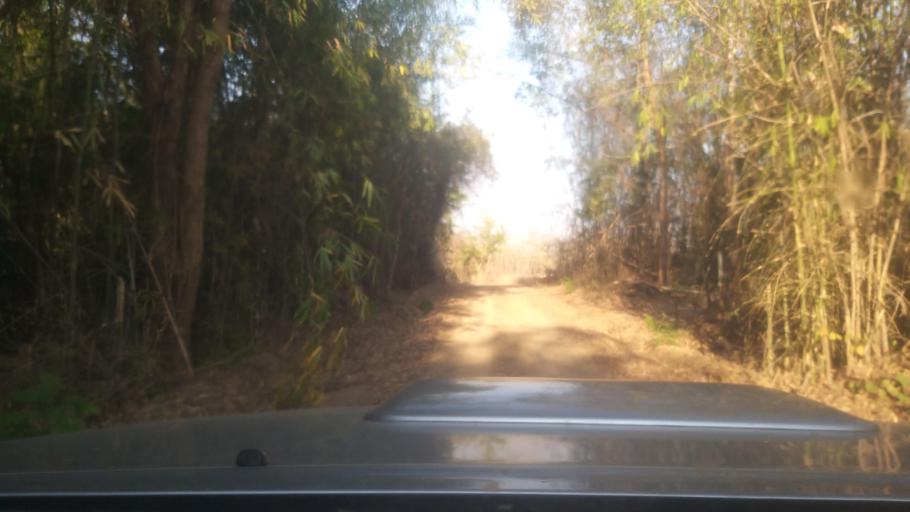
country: TH
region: Phrae
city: Nong Muang Khai
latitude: 18.2763
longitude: 100.0266
